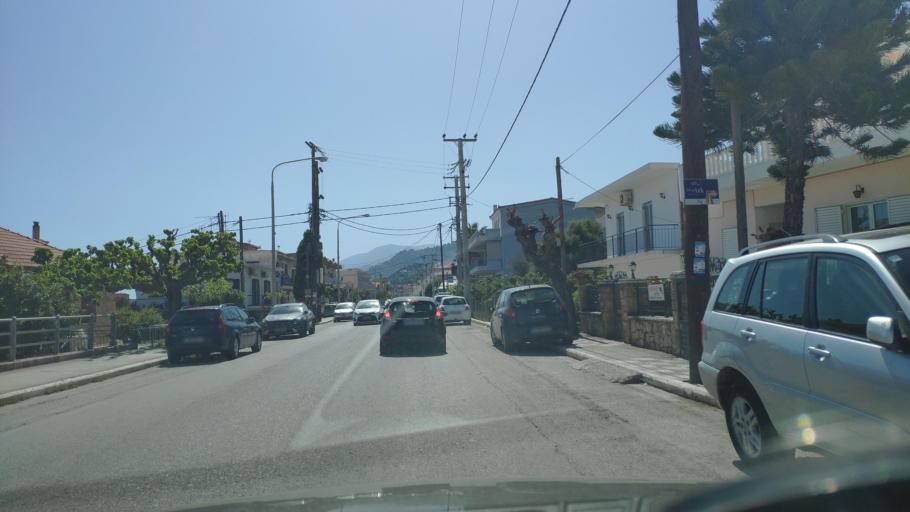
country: GR
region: West Greece
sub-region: Nomos Achaias
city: Aiyira
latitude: 38.1501
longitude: 22.3517
